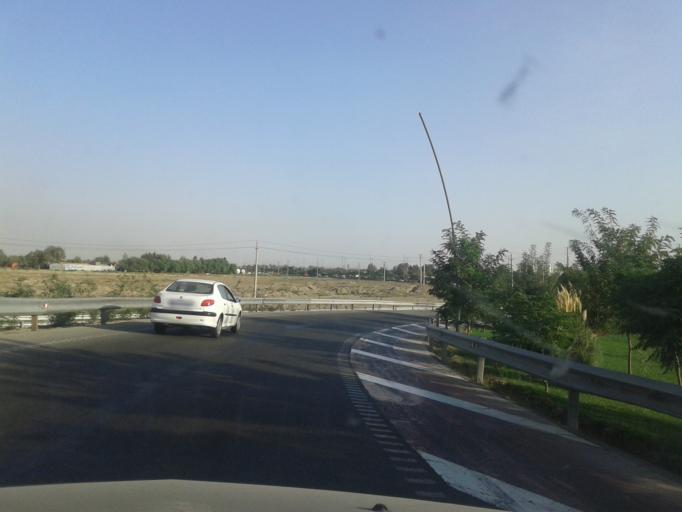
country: IR
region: Tehran
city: Eslamshahr
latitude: 35.6511
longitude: 51.2762
